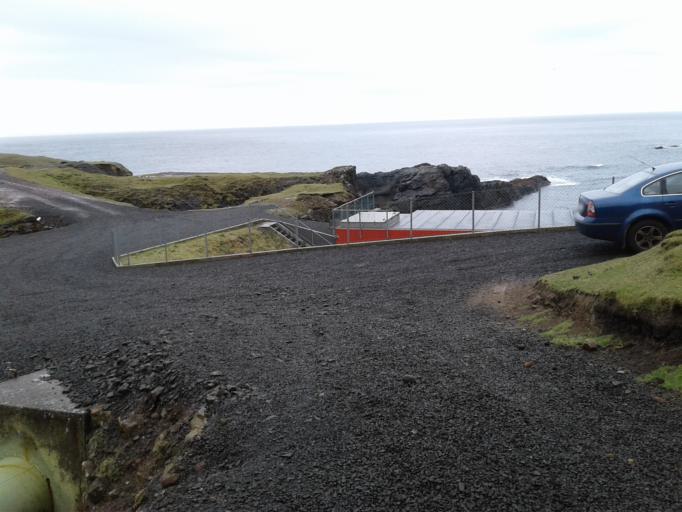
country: FO
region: Suduroy
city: Vagur
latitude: 61.4861
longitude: -6.8694
